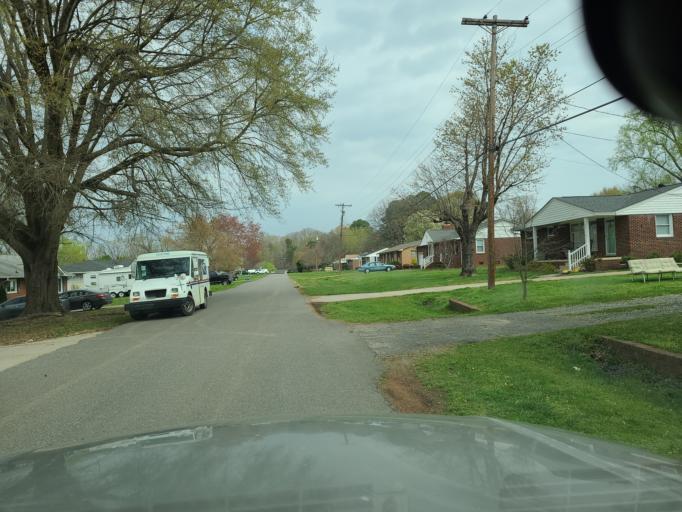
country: US
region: North Carolina
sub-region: Gaston County
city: Ranlo
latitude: 35.2805
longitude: -81.1378
